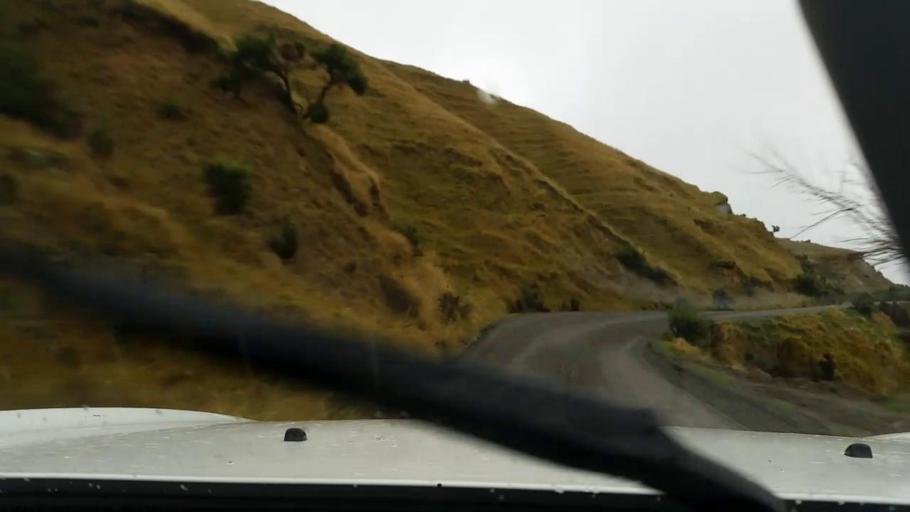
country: NZ
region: Wellington
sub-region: Masterton District
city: Masterton
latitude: -41.2501
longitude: 175.9071
